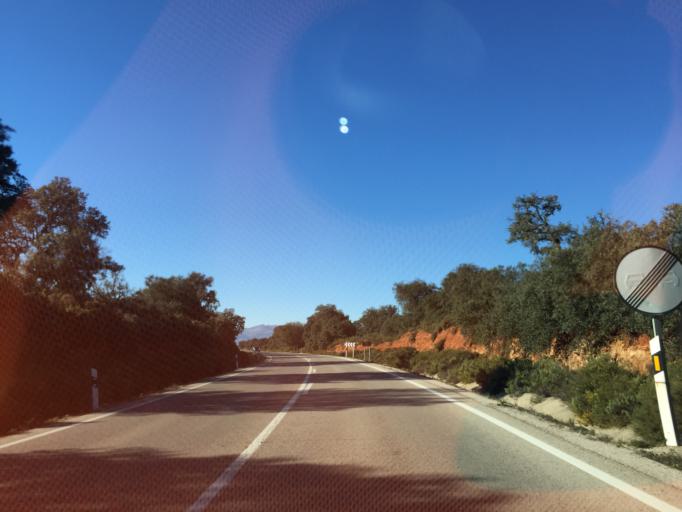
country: ES
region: Andalusia
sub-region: Provincia de Malaga
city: Arriate
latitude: 36.8236
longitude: -5.0955
